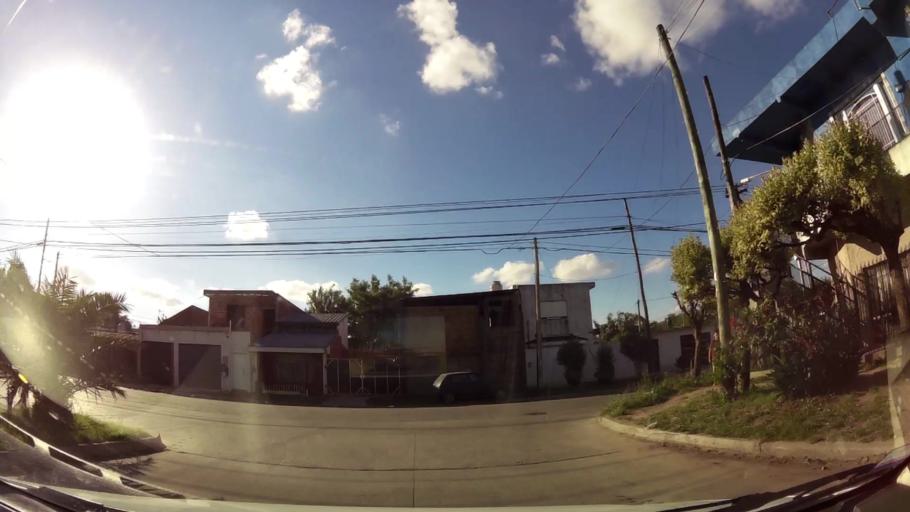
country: AR
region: Buenos Aires
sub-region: Partido de Moron
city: Moron
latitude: -34.6829
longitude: -58.6069
